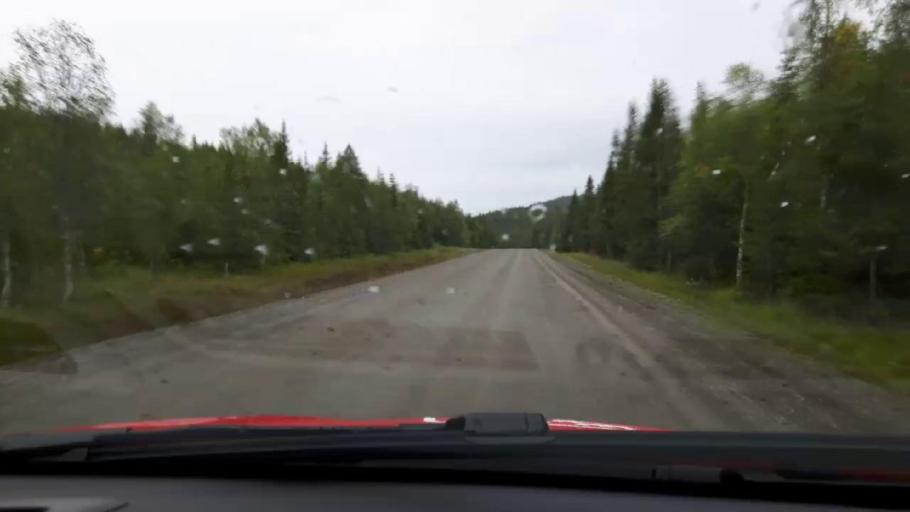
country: SE
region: Jaemtland
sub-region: Are Kommun
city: Are
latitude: 63.4275
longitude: 12.7386
